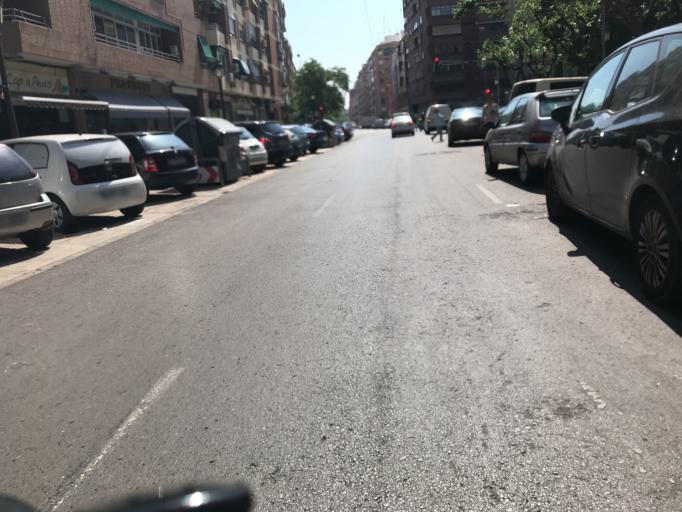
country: ES
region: Valencia
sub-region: Provincia de Valencia
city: Valencia
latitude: 39.4682
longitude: -0.3514
